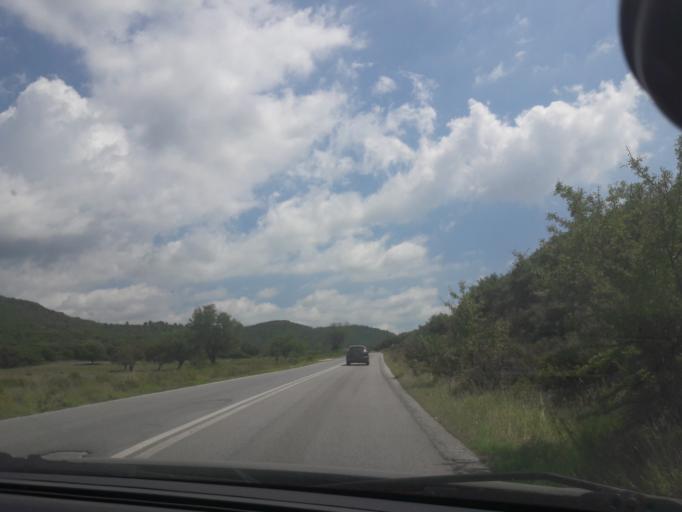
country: GR
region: Central Macedonia
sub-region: Nomos Chalkidikis
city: Polygyros
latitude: 40.3659
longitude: 23.4189
